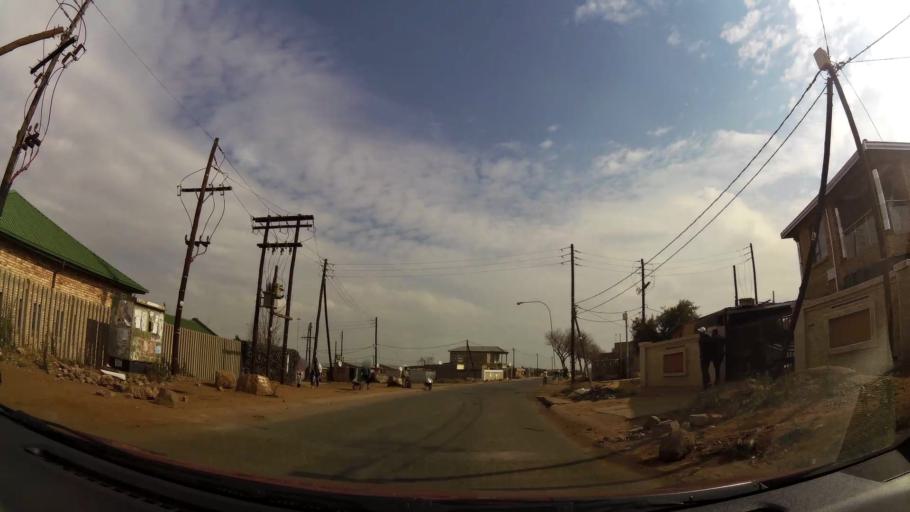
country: ZA
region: Gauteng
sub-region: City of Johannesburg Metropolitan Municipality
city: Soweto
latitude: -26.2596
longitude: 27.8202
